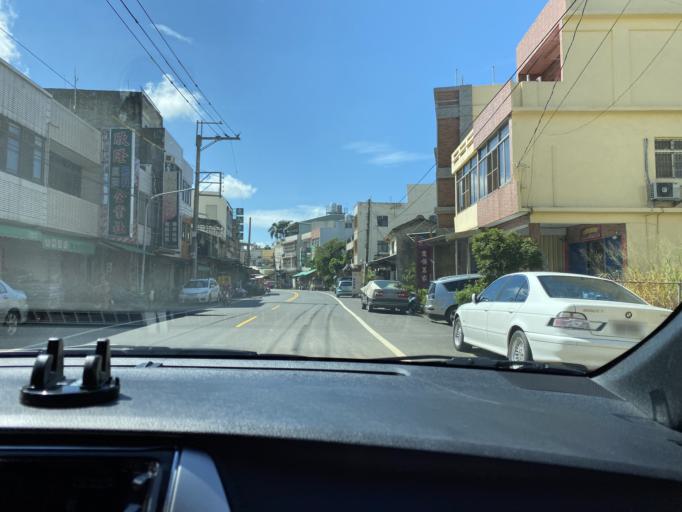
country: TW
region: Taiwan
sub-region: Nantou
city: Nantou
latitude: 23.8358
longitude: 120.6343
